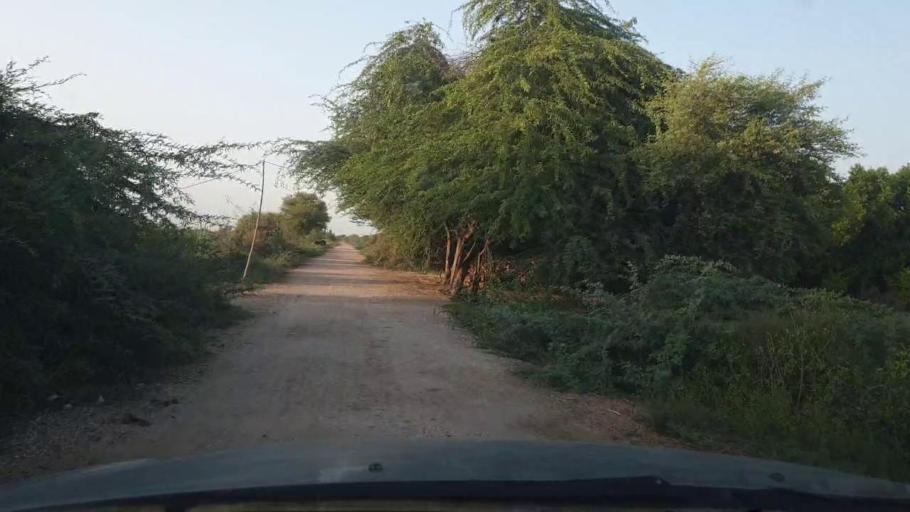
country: PK
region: Sindh
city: Tando Ghulam Ali
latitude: 25.1613
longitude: 68.9748
